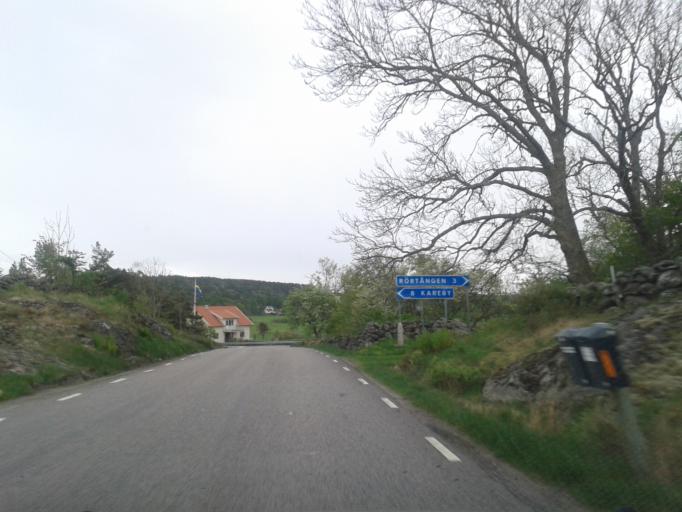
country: SE
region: Vaestra Goetaland
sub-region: Kungalvs Kommun
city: Kode
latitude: 57.9171
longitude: 11.8029
